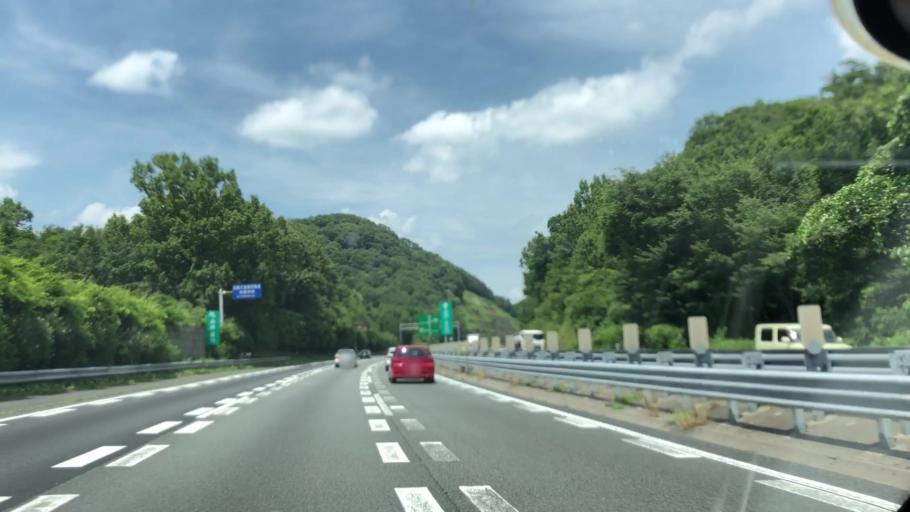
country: JP
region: Tochigi
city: Sano
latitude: 36.3294
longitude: 139.6141
